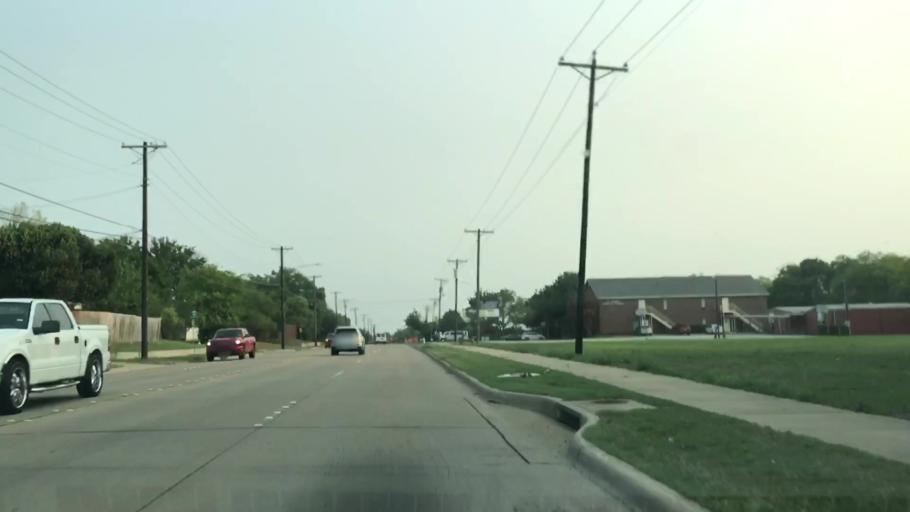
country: US
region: Texas
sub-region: Dallas County
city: Garland
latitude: 32.9067
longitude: -96.6214
